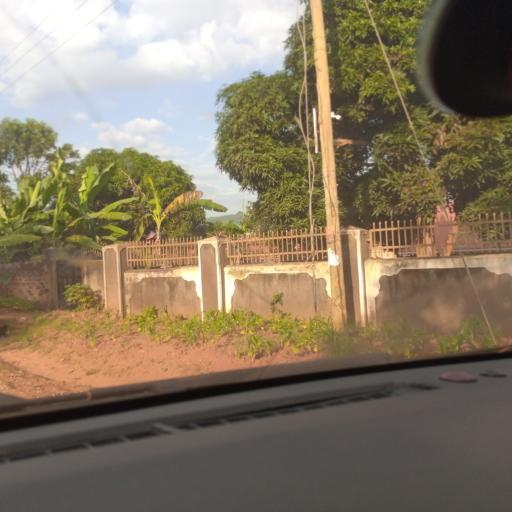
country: UG
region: Central Region
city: Masaka
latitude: -0.3467
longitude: 31.7249
